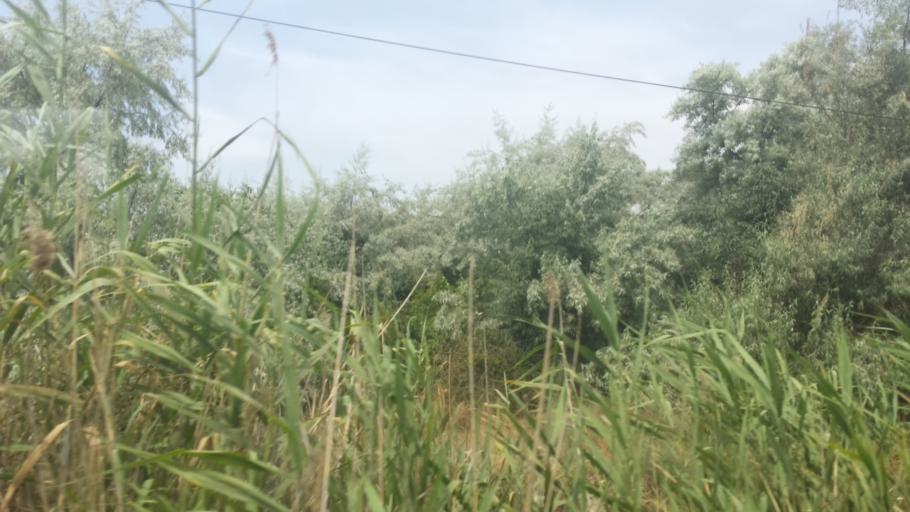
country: RO
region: Constanta
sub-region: Comuna Navodari
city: Navodari
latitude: 44.3242
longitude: 28.6197
